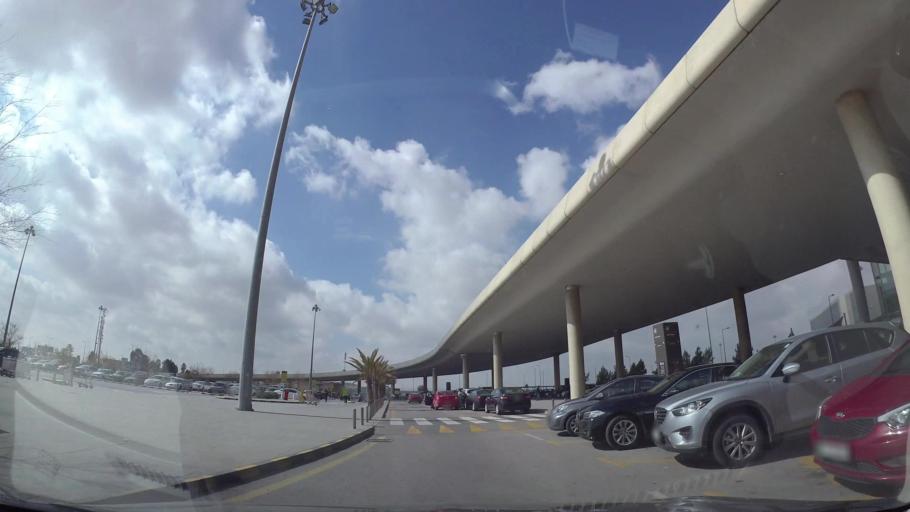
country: JO
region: Amman
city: Al Jizah
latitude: 31.7225
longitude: 35.9853
